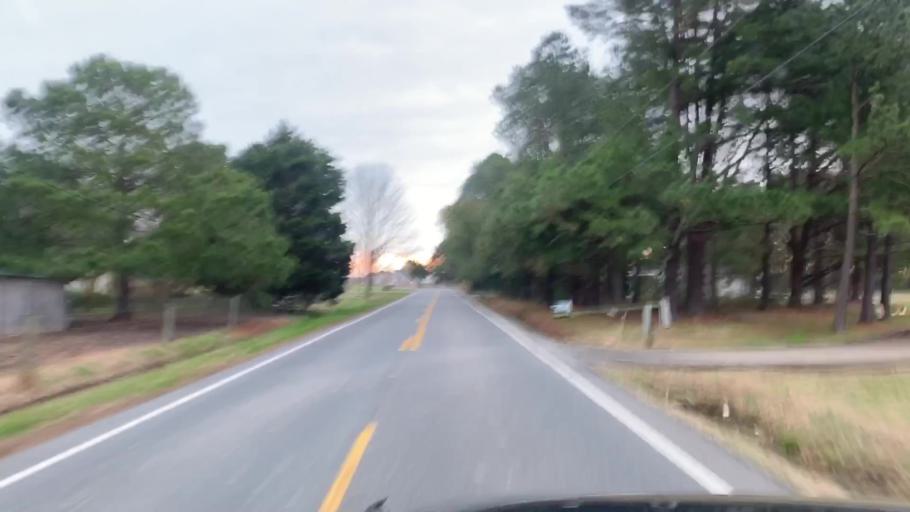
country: US
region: North Carolina
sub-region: Currituck County
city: Moyock
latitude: 36.6247
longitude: -76.1607
